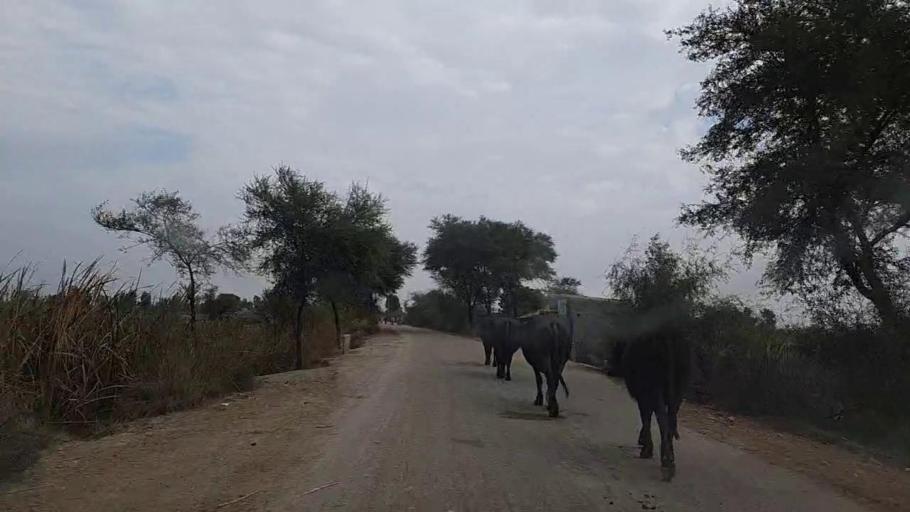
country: PK
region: Sindh
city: Sanghar
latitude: 26.2284
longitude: 69.0129
